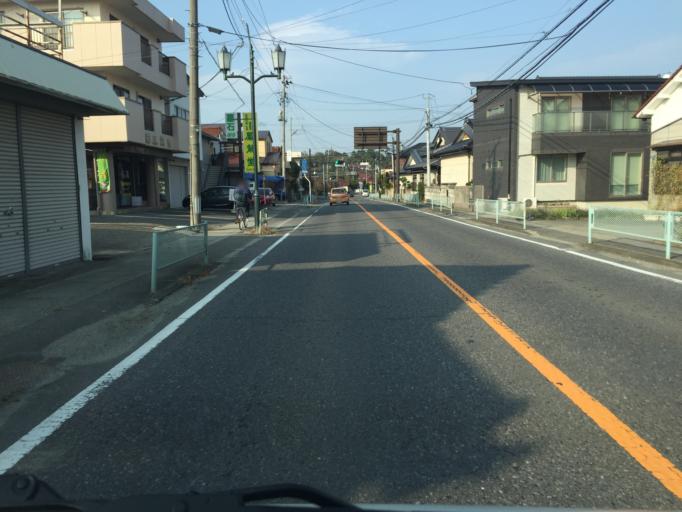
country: JP
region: Fukushima
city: Koriyama
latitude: 37.4265
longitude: 140.3920
